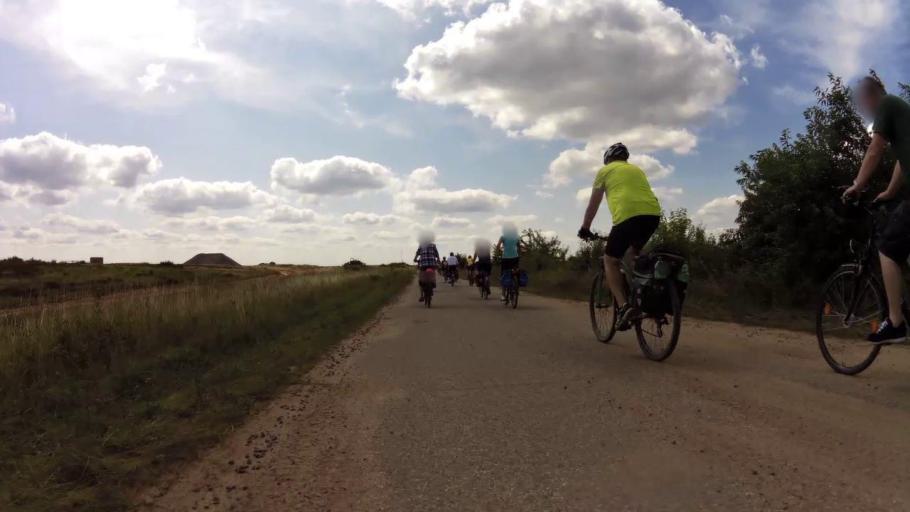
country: PL
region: West Pomeranian Voivodeship
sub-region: Powiat drawski
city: Drawsko Pomorskie
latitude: 53.4338
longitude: 15.7615
